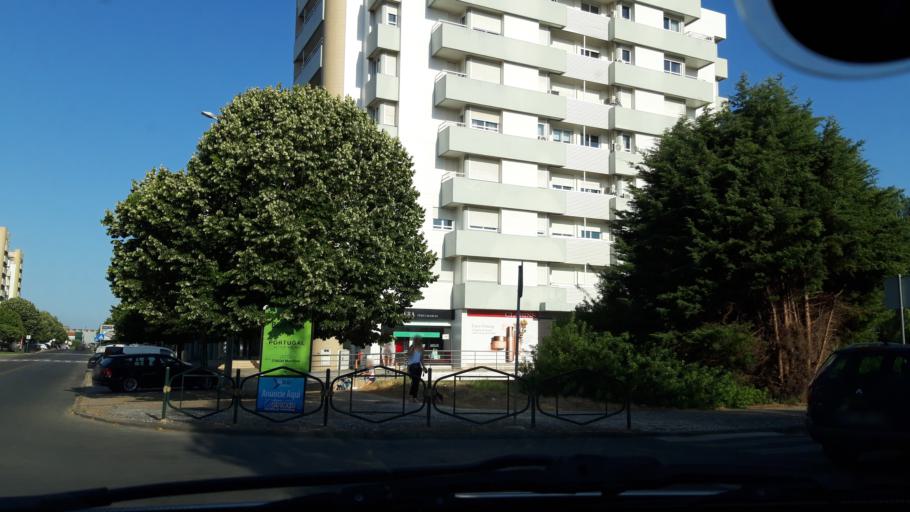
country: PT
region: Santarem
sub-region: Torres Novas
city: Torres Novas
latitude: 39.4737
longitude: -8.5449
